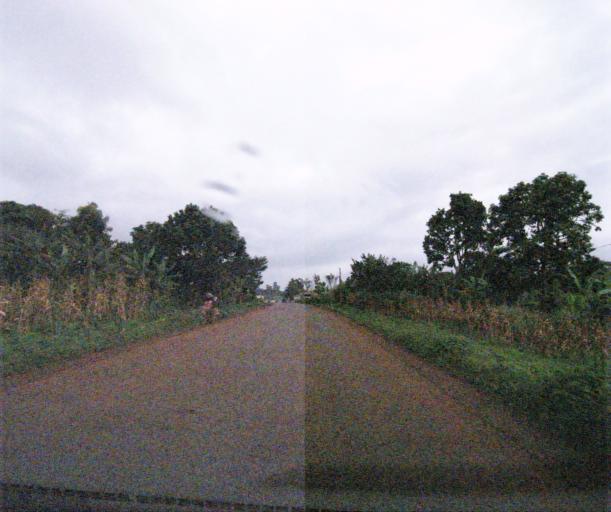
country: CM
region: West
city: Bansoa
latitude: 5.5007
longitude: 10.2383
